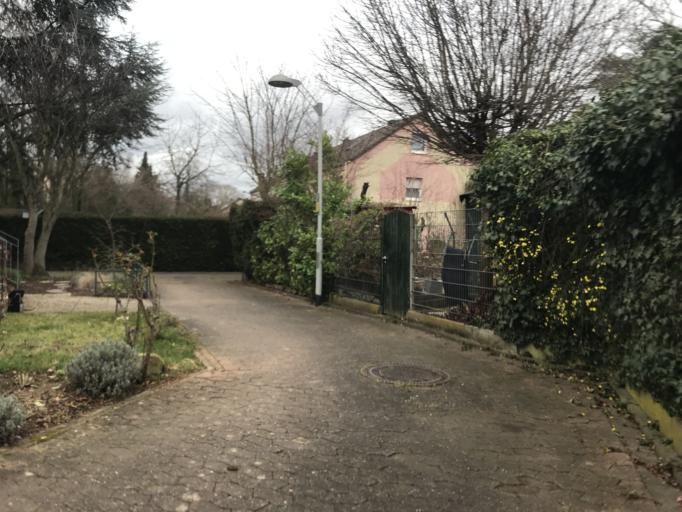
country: DE
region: Rheinland-Pfalz
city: Mainz
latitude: 49.9741
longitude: 8.2454
